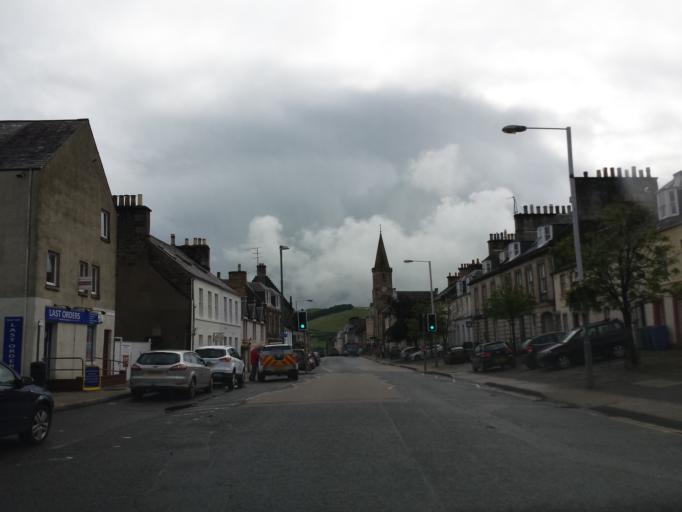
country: GB
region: Scotland
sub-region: Fife
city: Newburgh
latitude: 56.3507
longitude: -3.2411
